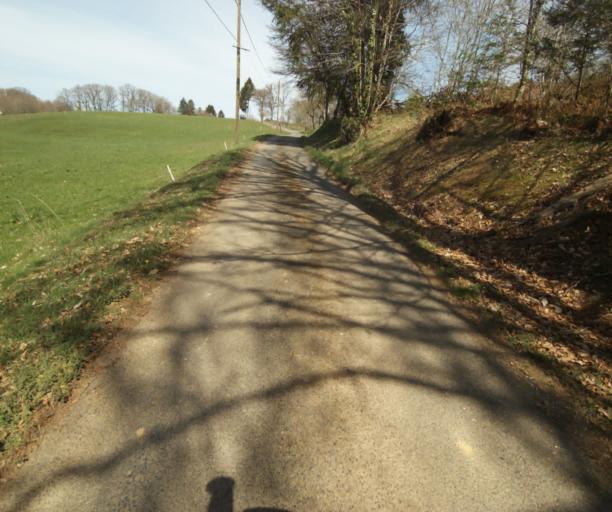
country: FR
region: Limousin
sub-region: Departement de la Correze
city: Seilhac
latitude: 45.4031
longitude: 1.7730
